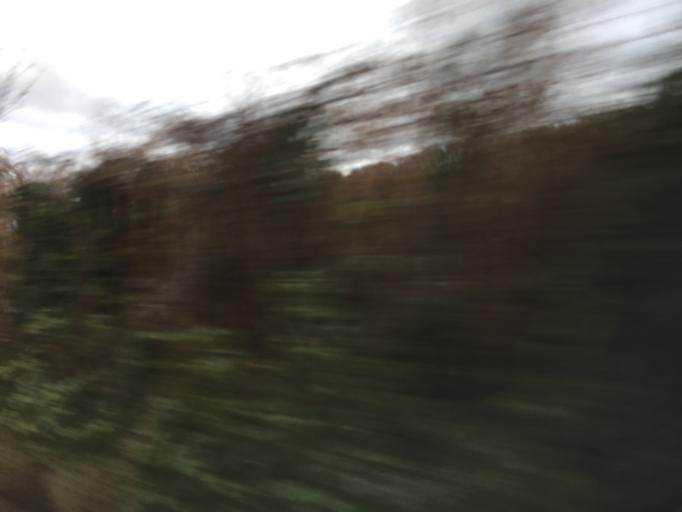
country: GB
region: Wales
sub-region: Monmouthshire
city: Magor
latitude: 51.5988
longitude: -2.8257
